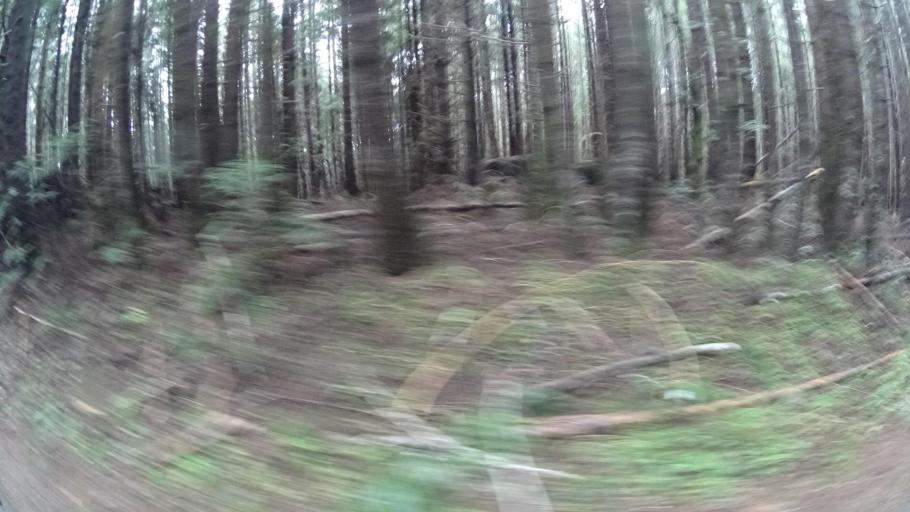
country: US
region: California
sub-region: Humboldt County
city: Westhaven-Moonstone
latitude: 41.2424
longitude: -123.9831
